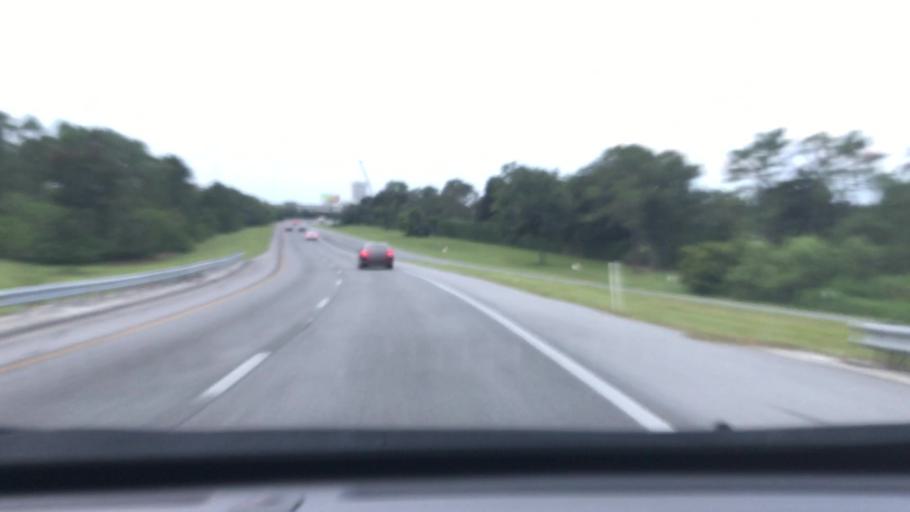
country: US
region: Florida
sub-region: Osceola County
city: Celebration
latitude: 28.3602
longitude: -81.5160
